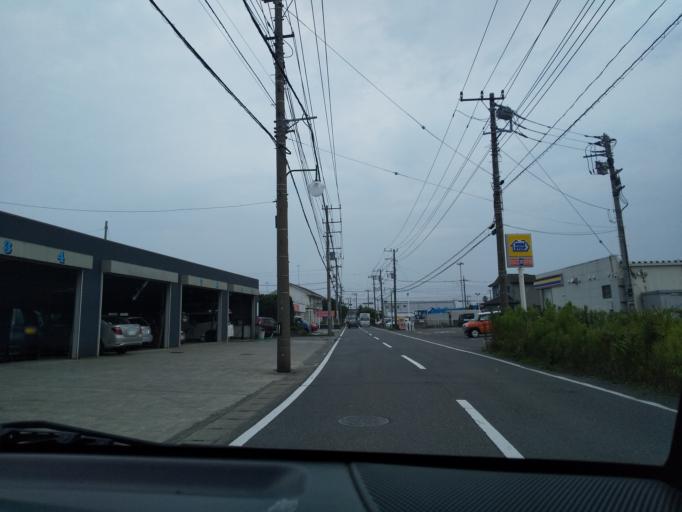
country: JP
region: Kanagawa
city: Atsugi
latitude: 35.3999
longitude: 139.3853
